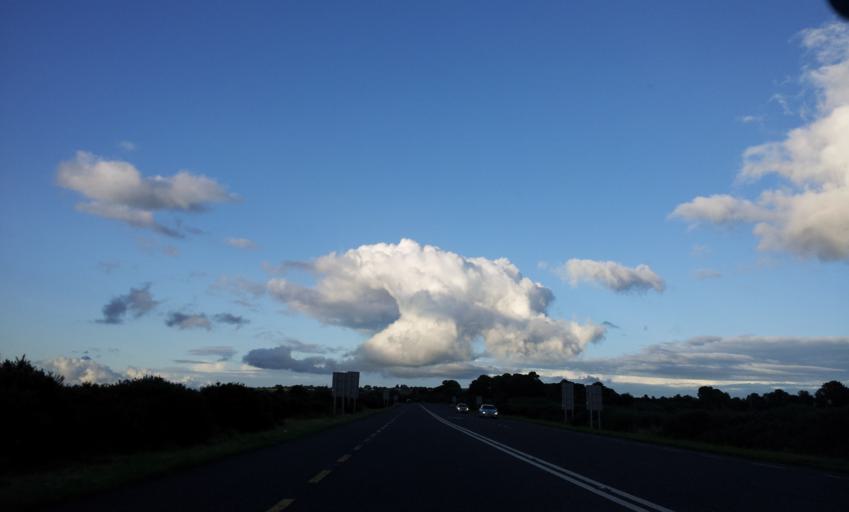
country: IE
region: Munster
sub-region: County Limerick
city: Abbeyfeale
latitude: 52.3458
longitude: -9.3390
